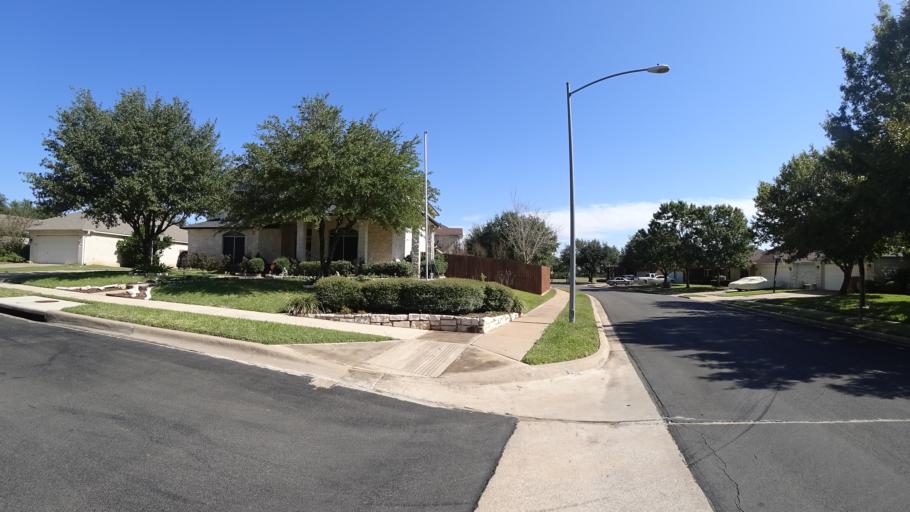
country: US
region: Texas
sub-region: Travis County
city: Shady Hollow
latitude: 30.1933
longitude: -97.8617
